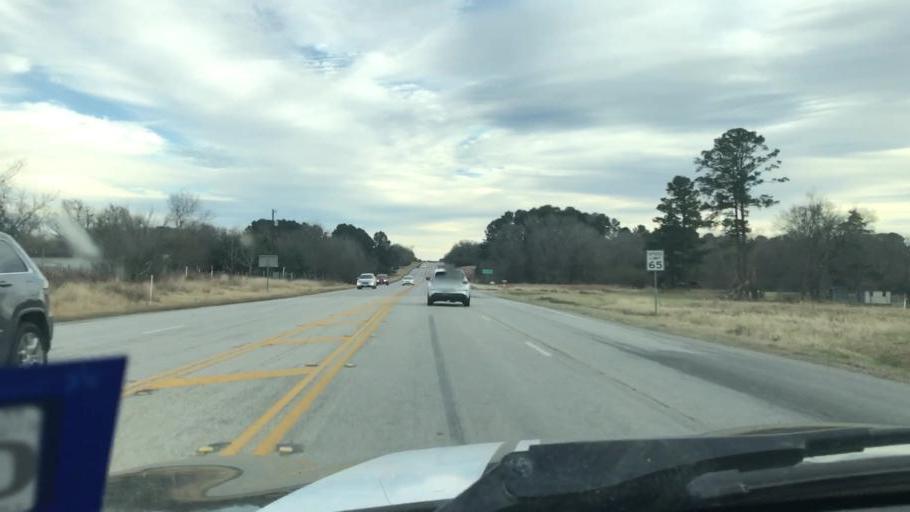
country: US
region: Texas
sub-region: Bastrop County
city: Camp Swift
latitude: 30.2779
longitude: -97.2413
